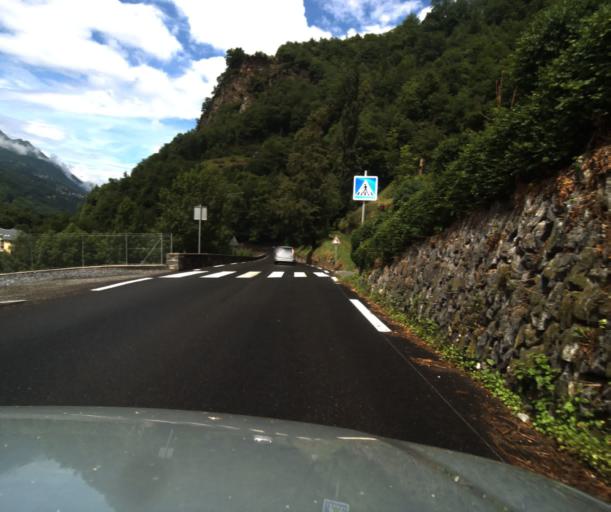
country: FR
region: Midi-Pyrenees
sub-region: Departement des Hautes-Pyrenees
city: Luz-Saint-Sauveur
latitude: 42.8613
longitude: -0.0059
